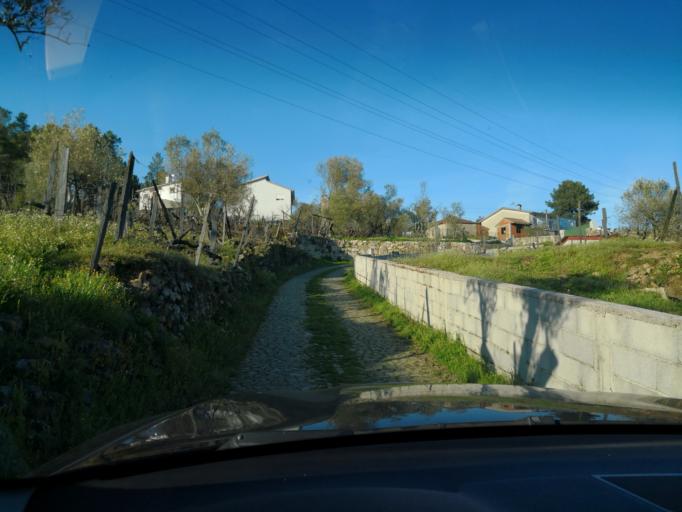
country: PT
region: Vila Real
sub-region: Vila Real
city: Vila Real
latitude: 41.2880
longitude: -7.7888
